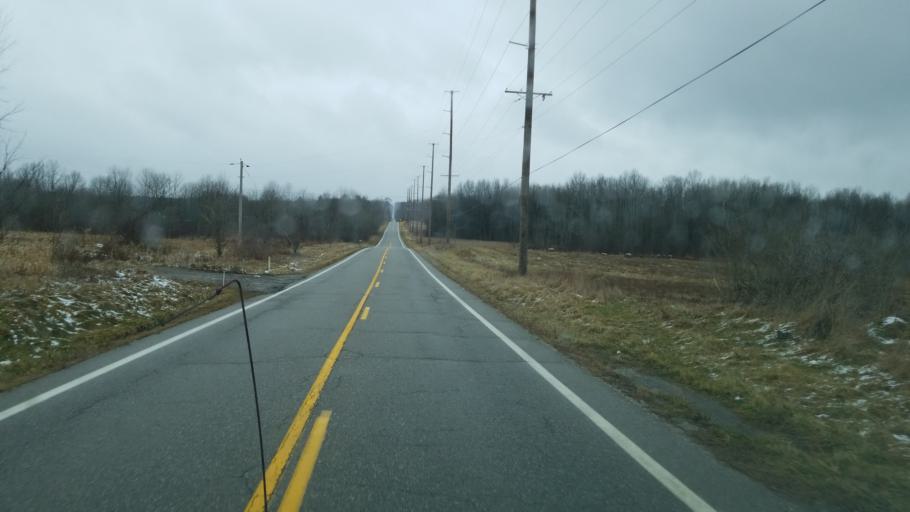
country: US
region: Ohio
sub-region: Portage County
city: Windham
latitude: 41.3100
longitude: -81.0040
